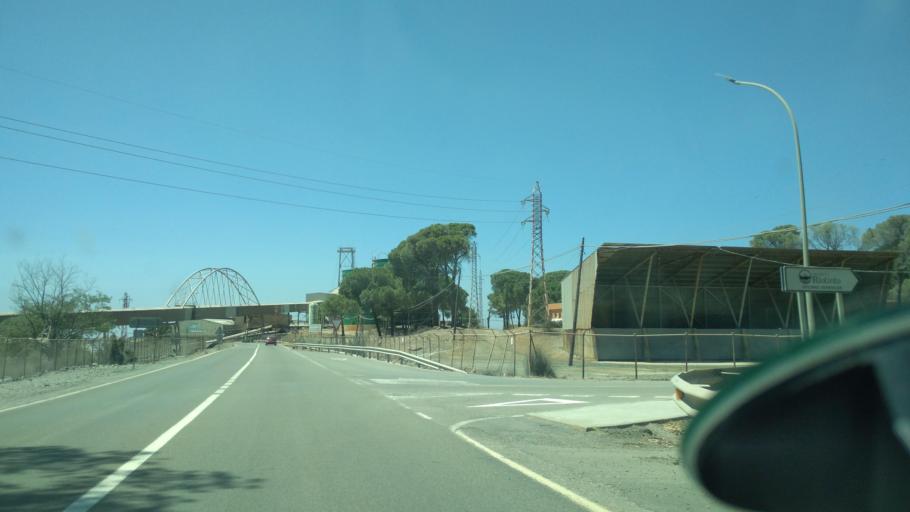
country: ES
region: Andalusia
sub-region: Provincia de Huelva
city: Nerva
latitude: 37.7126
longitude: -6.5834
